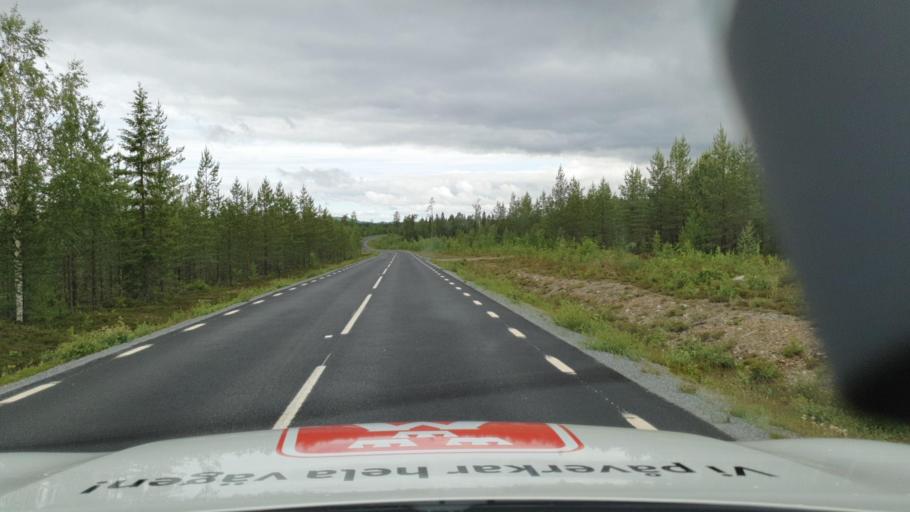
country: SE
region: Vaesterbotten
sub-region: Dorotea Kommun
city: Dorotea
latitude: 64.1929
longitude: 16.5885
